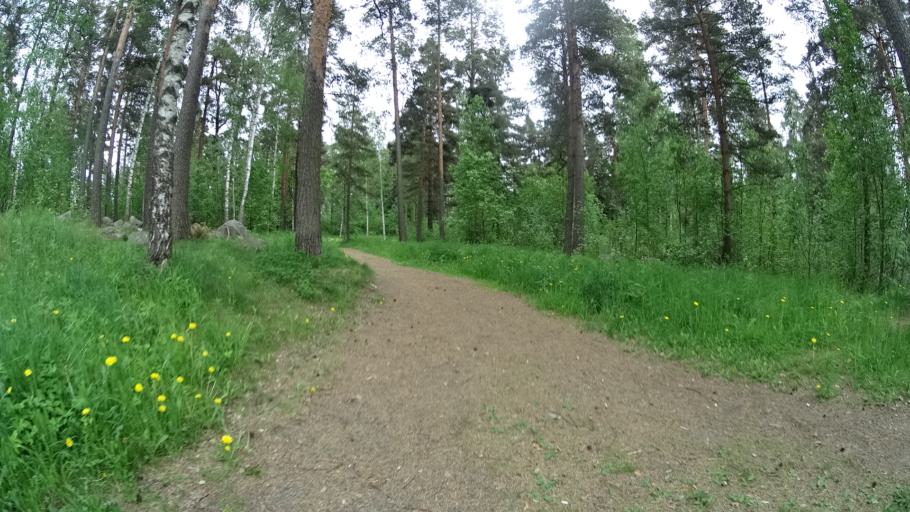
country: FI
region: Uusimaa
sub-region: Helsinki
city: Vantaa
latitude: 60.2959
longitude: 25.0533
